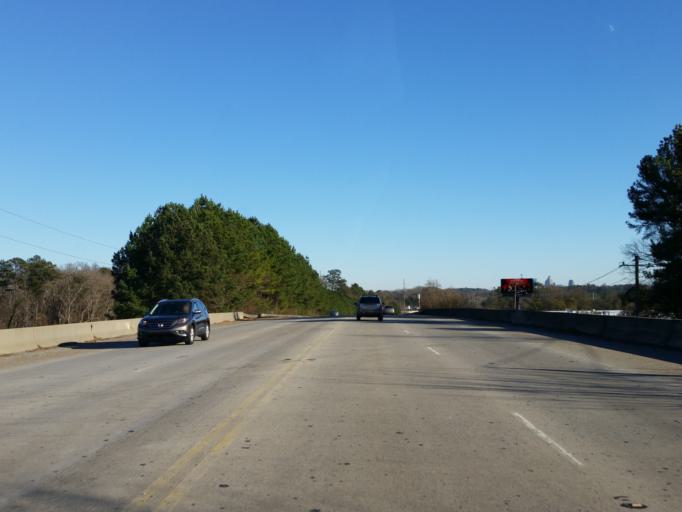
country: US
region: Georgia
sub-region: Cobb County
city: Vinings
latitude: 33.8342
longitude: -84.4663
